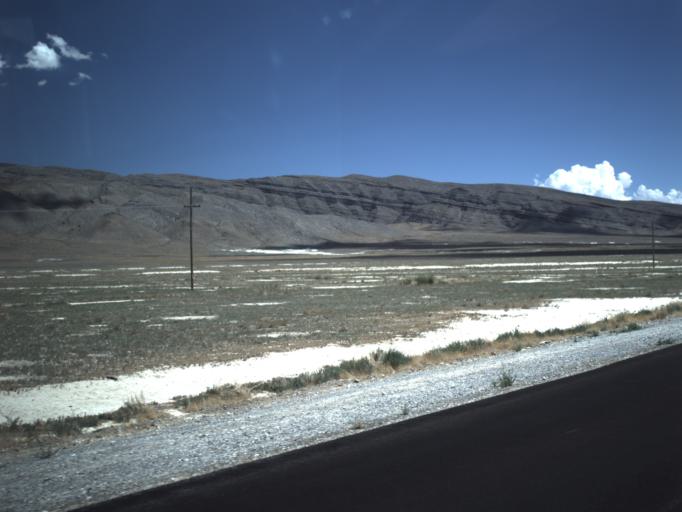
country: US
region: Utah
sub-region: Beaver County
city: Milford
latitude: 39.0659
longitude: -113.4499
